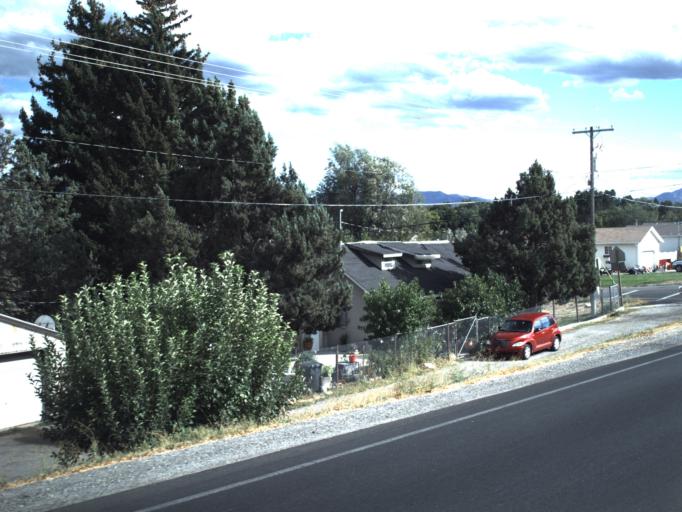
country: US
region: Utah
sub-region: Cache County
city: Hyrum
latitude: 41.6349
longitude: -111.8664
